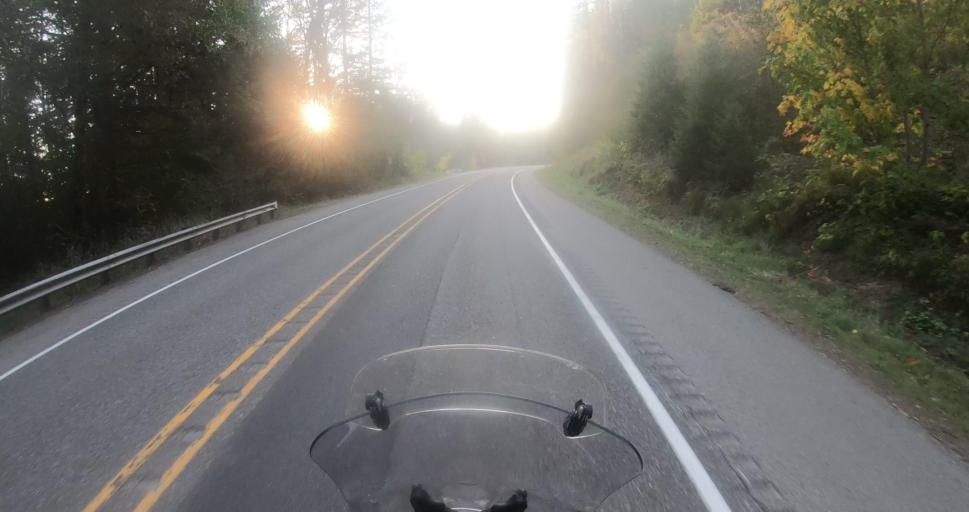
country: US
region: Washington
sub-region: Lewis County
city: Morton
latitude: 46.5360
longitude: -122.0056
